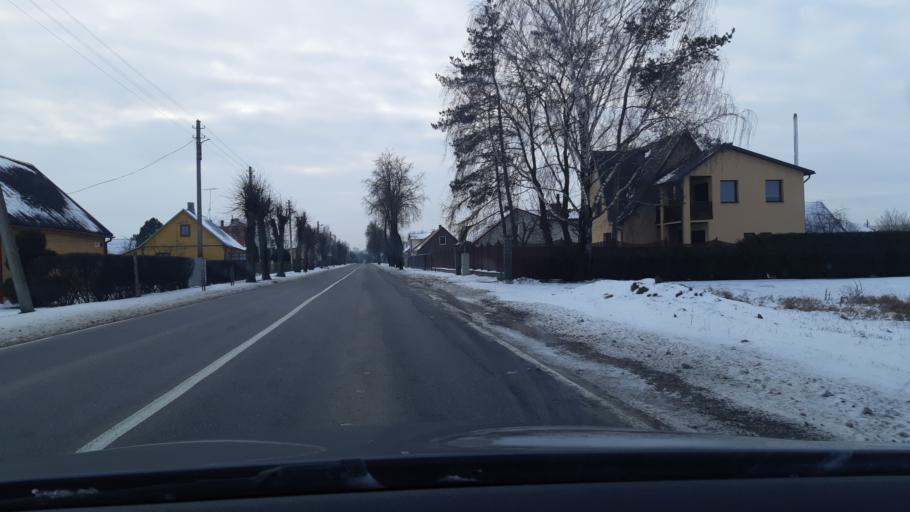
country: LT
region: Kauno apskritis
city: Kedainiai
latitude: 55.2476
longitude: 23.8444
